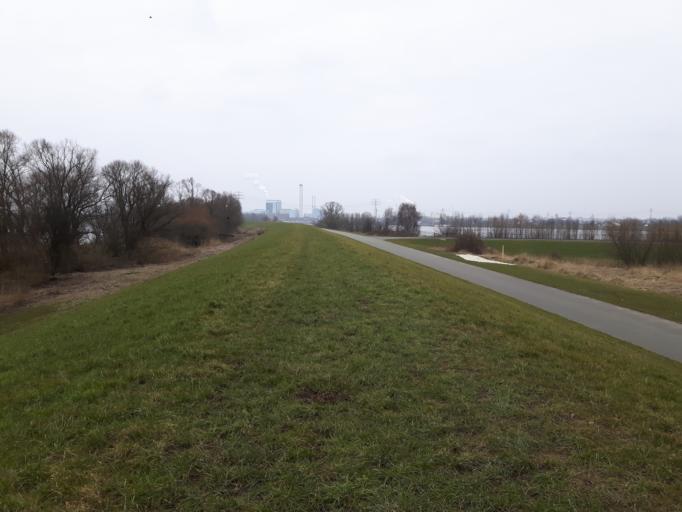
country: DE
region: Hamburg
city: Rothenburgsort
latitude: 53.5099
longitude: 10.0622
